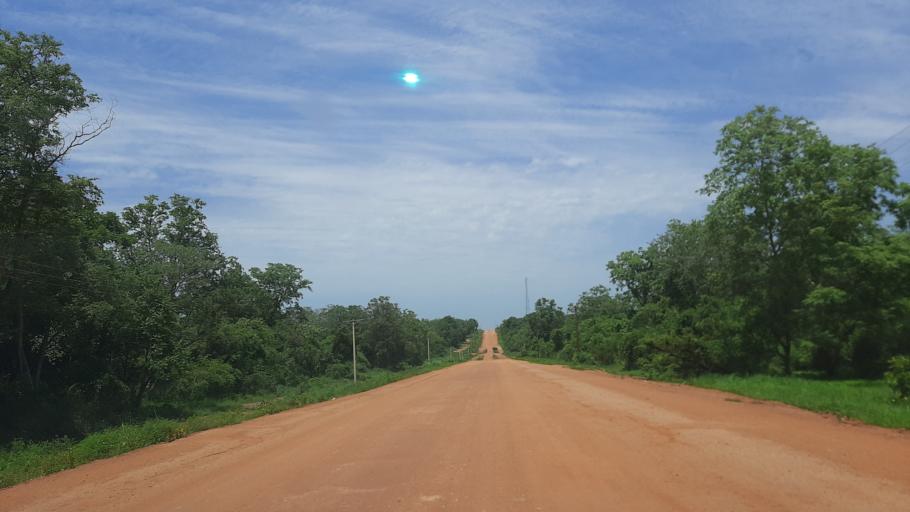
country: ET
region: Gambela
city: Gambela
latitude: 8.0701
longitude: 34.5880
